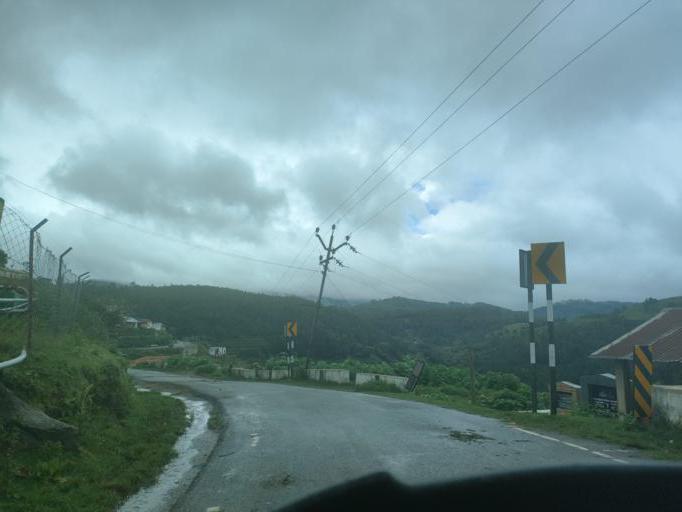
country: IN
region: Tamil Nadu
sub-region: Dindigul
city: Kodaikanal
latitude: 10.2230
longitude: 77.3455
